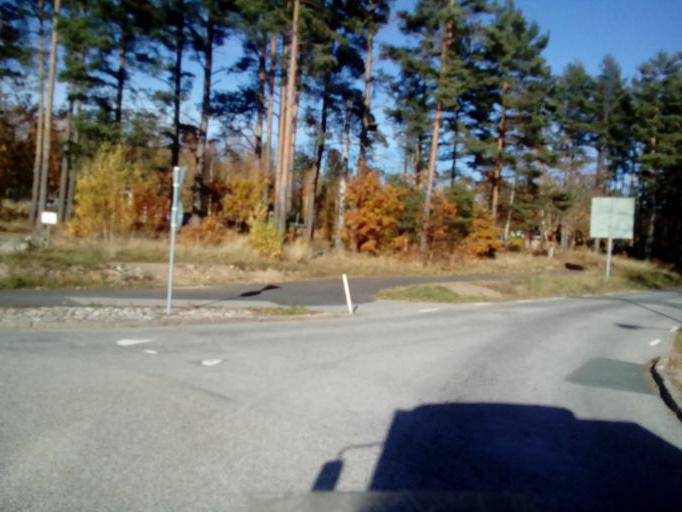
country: SE
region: Kalmar
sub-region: Vimmerby Kommun
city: Vimmerby
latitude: 57.6728
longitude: 15.8721
